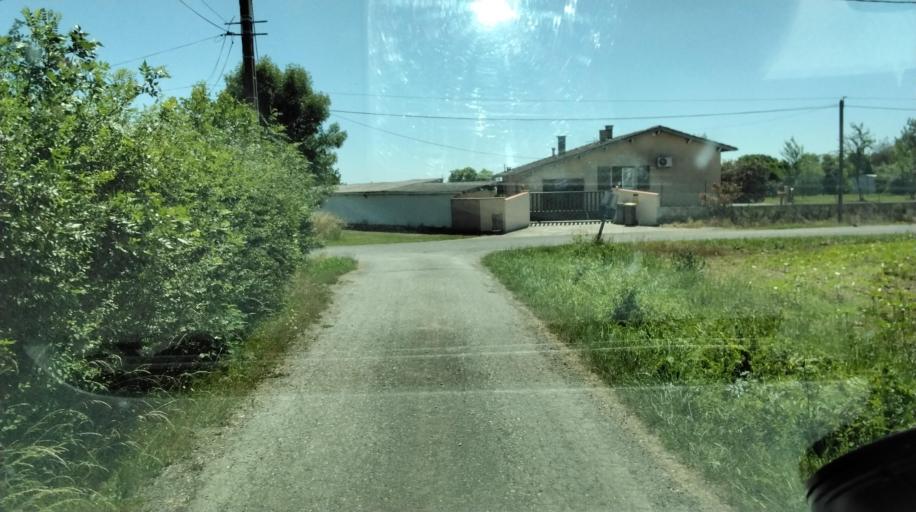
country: FR
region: Midi-Pyrenees
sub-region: Departement de la Haute-Garonne
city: Sainte-Foy-de-Peyrolieres
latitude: 43.4848
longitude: 1.1199
